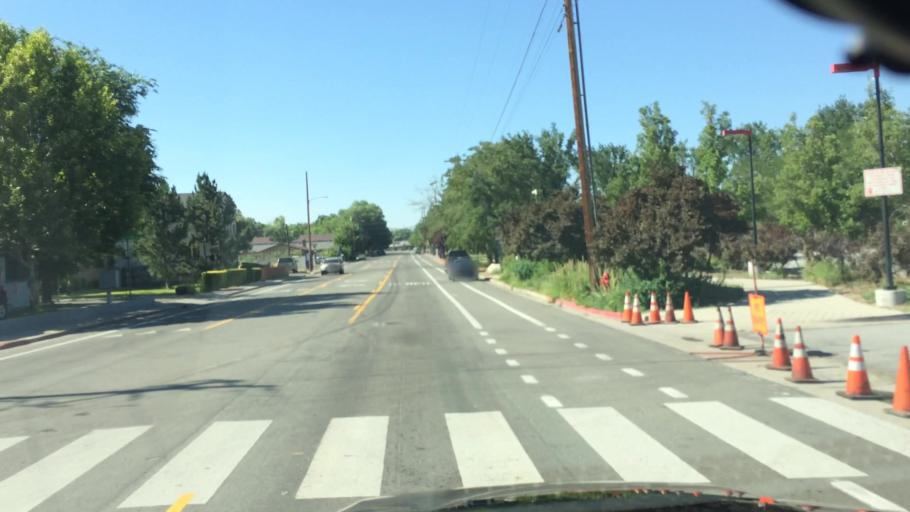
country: US
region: Nevada
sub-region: Washoe County
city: Reno
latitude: 39.4885
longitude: -119.7804
